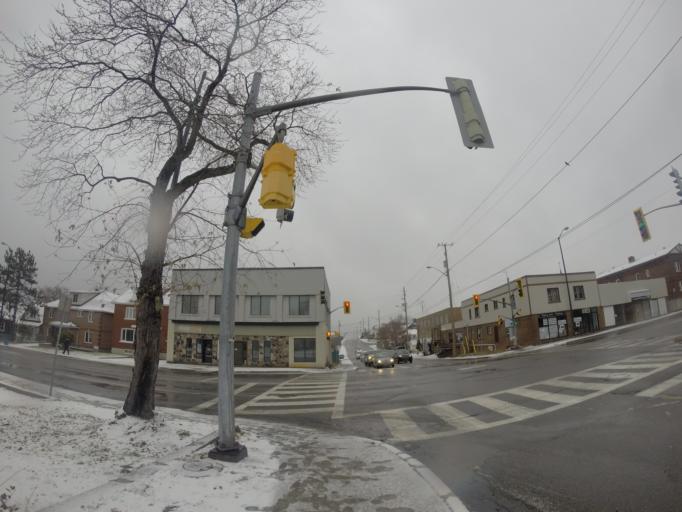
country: CA
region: Ontario
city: Greater Sudbury
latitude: 46.4933
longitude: -81.0068
